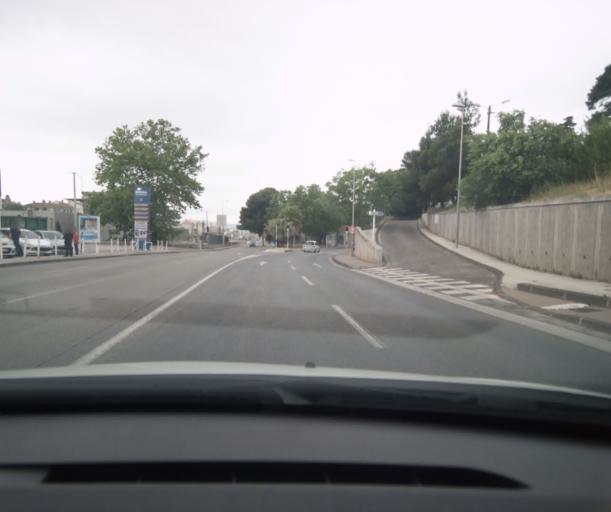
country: FR
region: Provence-Alpes-Cote d'Azur
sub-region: Departement du Var
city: Toulon
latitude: 43.1266
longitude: 5.9359
